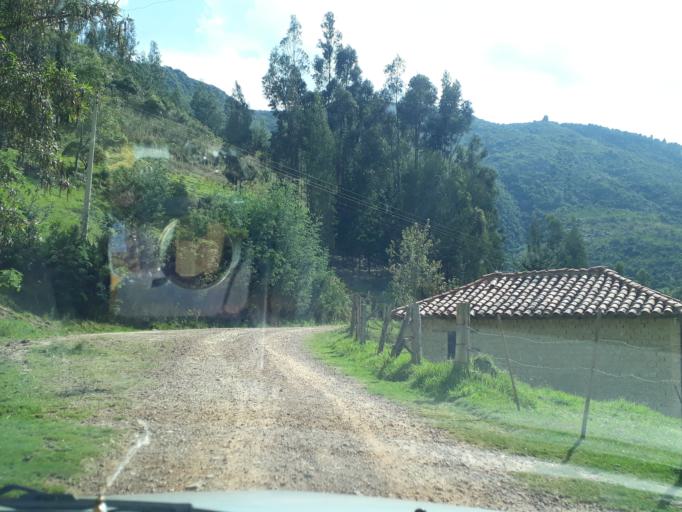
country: CO
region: Boyaca
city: Santa Rosa de Viterbo
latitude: 5.8525
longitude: -72.9626
